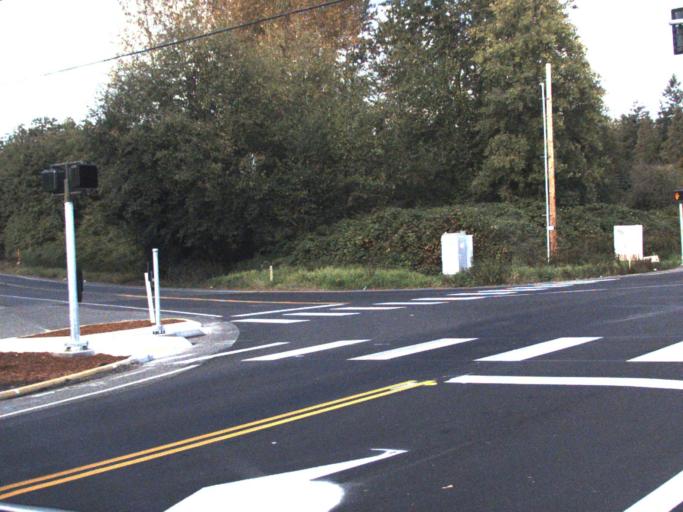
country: US
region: Washington
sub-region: Skagit County
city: Sedro-Woolley
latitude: 48.4926
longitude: -122.2802
